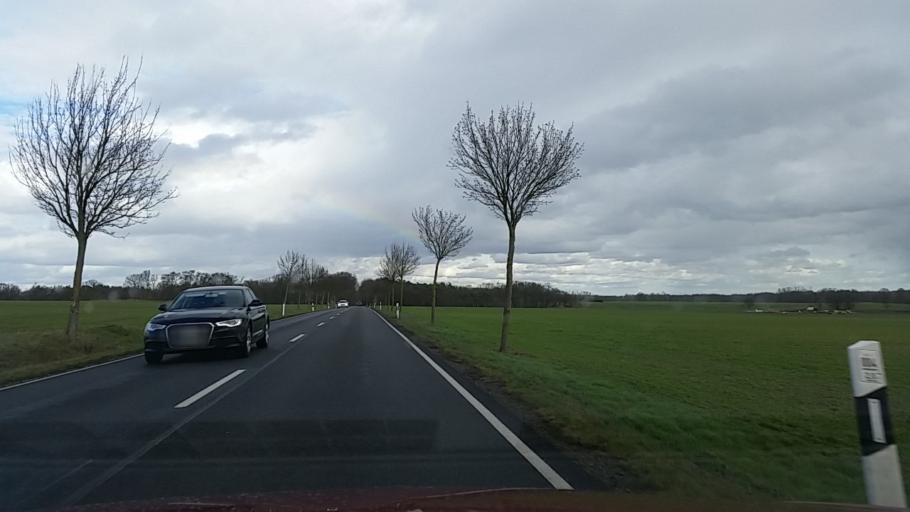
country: DE
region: Saxony-Anhalt
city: Rohrberg
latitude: 52.7248
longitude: 11.0543
